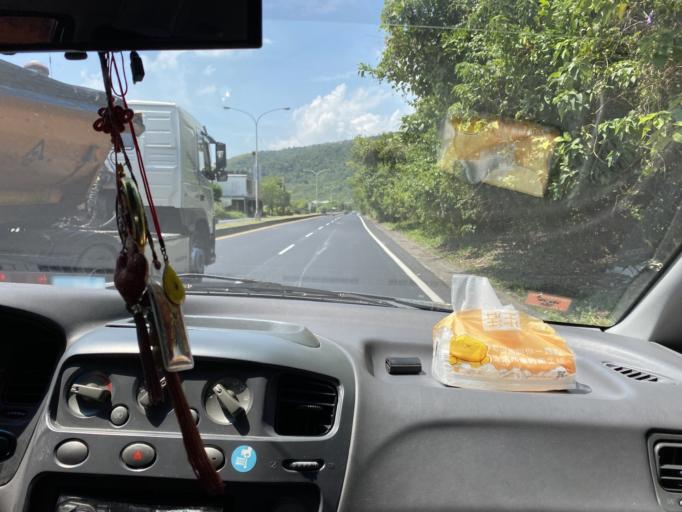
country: TW
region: Taiwan
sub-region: Yilan
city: Yilan
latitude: 24.8933
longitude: 121.8561
